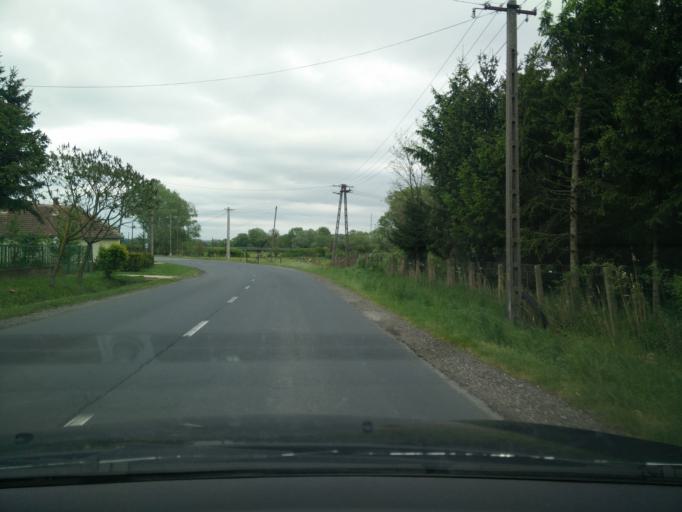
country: HU
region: Zala
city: Zalaszentgrot
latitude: 46.9783
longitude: 17.0212
